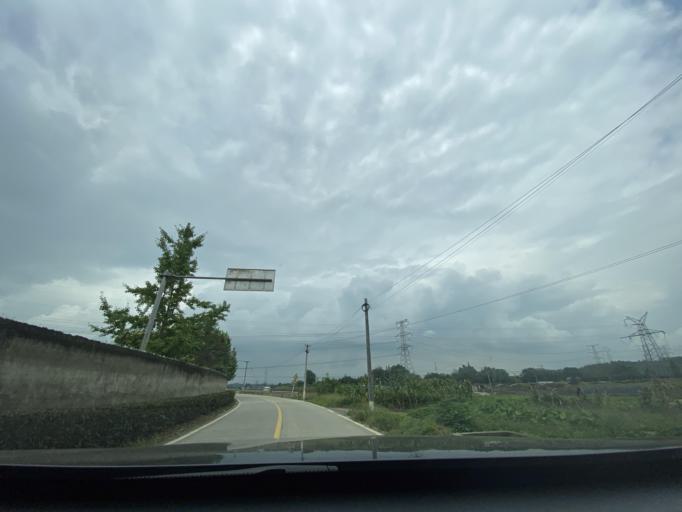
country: CN
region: Sichuan
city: Wujin
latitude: 30.3728
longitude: 103.9701
